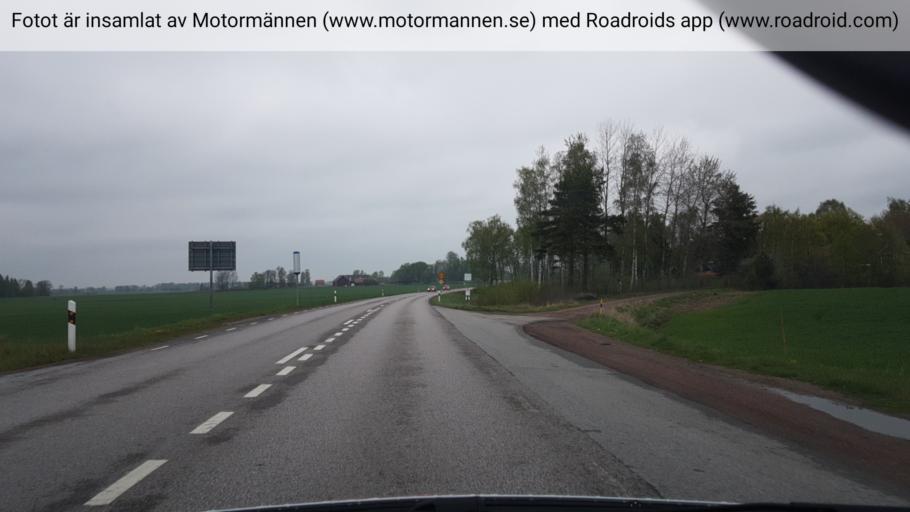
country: SE
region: Vaestra Goetaland
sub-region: Skovde Kommun
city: Stopen
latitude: 58.4751
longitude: 13.9548
